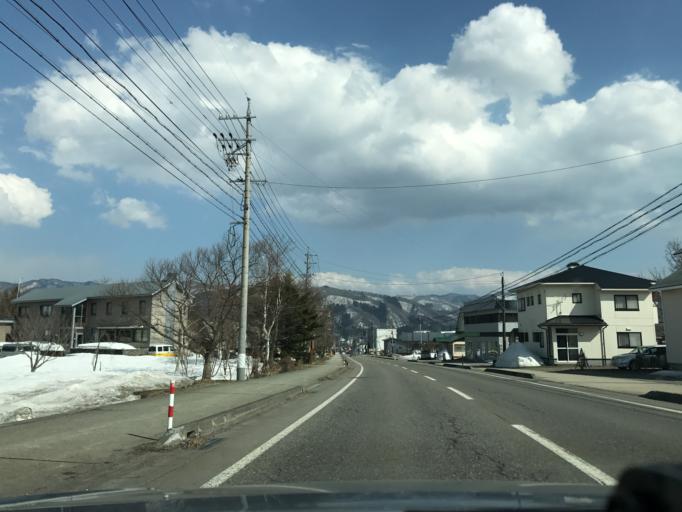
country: JP
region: Nagano
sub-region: Kitaazumi Gun
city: Hakuba
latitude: 36.7005
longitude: 137.8498
